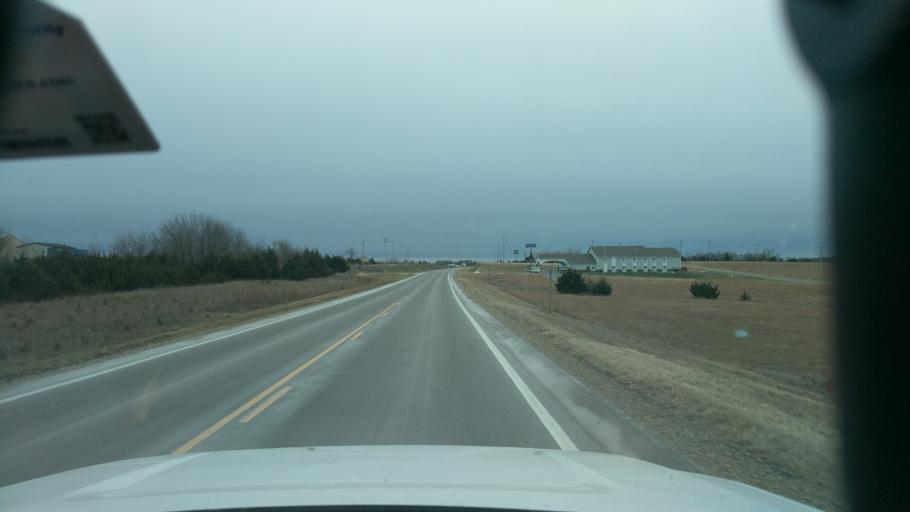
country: US
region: Kansas
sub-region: Dickinson County
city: Herington
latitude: 38.6803
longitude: -96.9305
